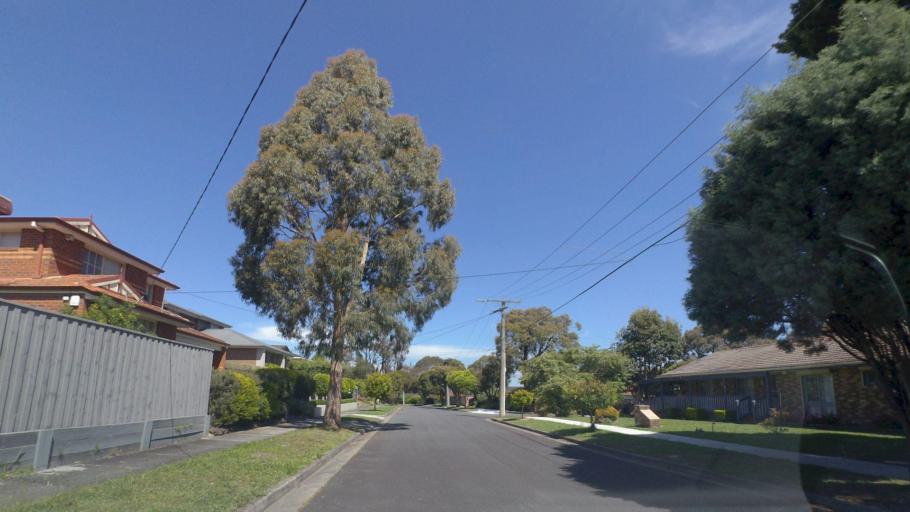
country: AU
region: Victoria
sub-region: Whitehorse
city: Vermont South
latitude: -37.8513
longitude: 145.1927
